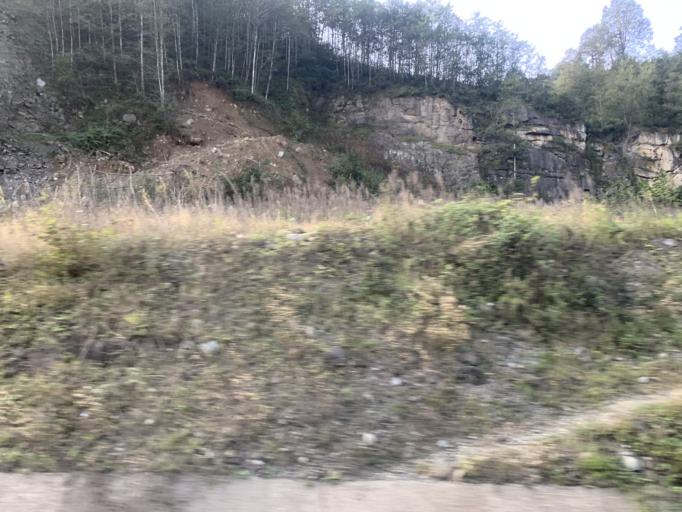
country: TR
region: Trabzon
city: Of
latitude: 40.8784
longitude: 40.2815
